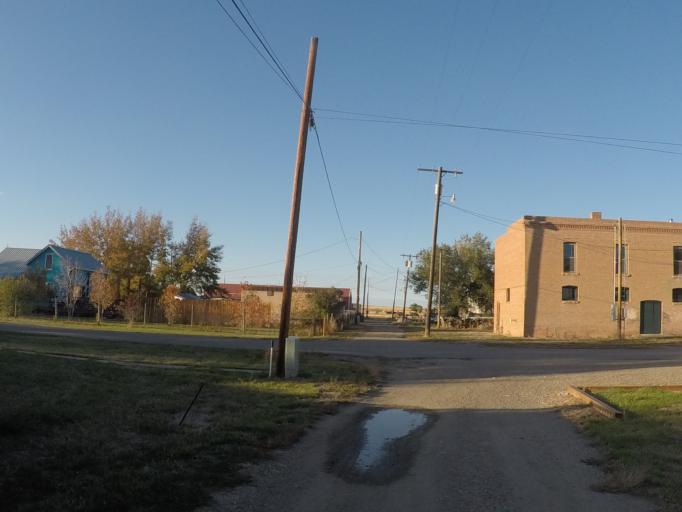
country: US
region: Montana
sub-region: Golden Valley County
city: Ryegate
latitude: 46.2941
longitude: -108.9387
